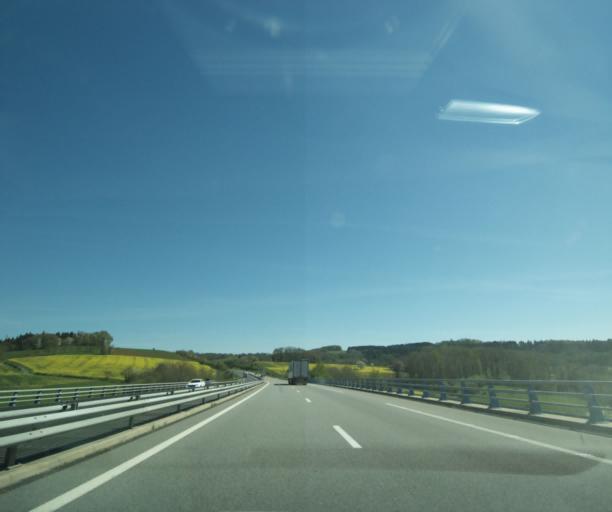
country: FR
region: Limousin
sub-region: Departement de la Correze
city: Vigeois
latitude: 45.4110
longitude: 1.5274
